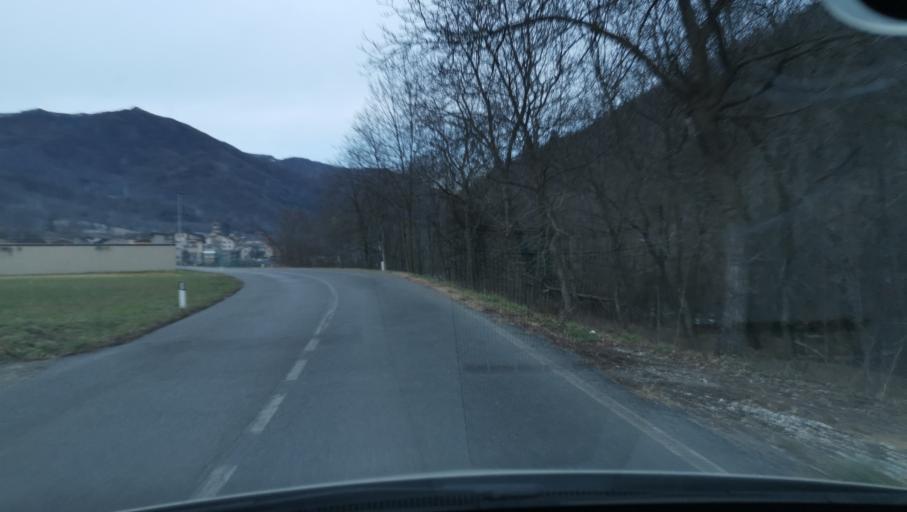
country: IT
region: Piedmont
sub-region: Provincia di Cuneo
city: Monterosso Grana
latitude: 44.4099
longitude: 7.3299
